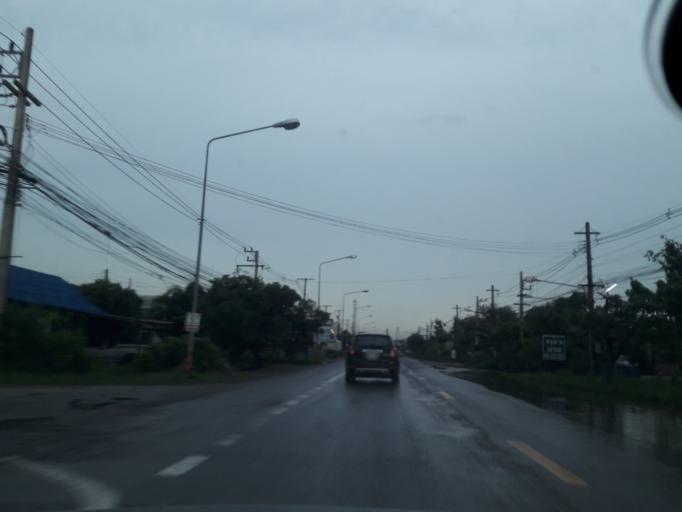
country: TH
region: Pathum Thani
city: Lam Luk Ka
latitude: 13.9426
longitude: 100.7464
